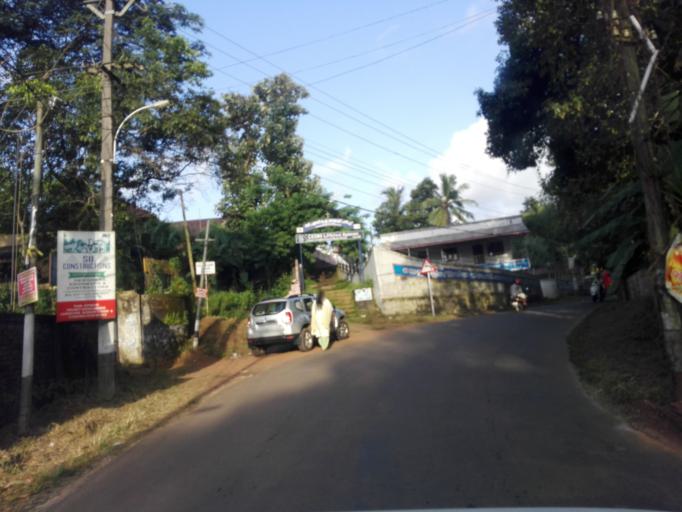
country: IN
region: Kerala
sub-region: Kottayam
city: Kottayam
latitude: 9.6123
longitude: 76.4987
